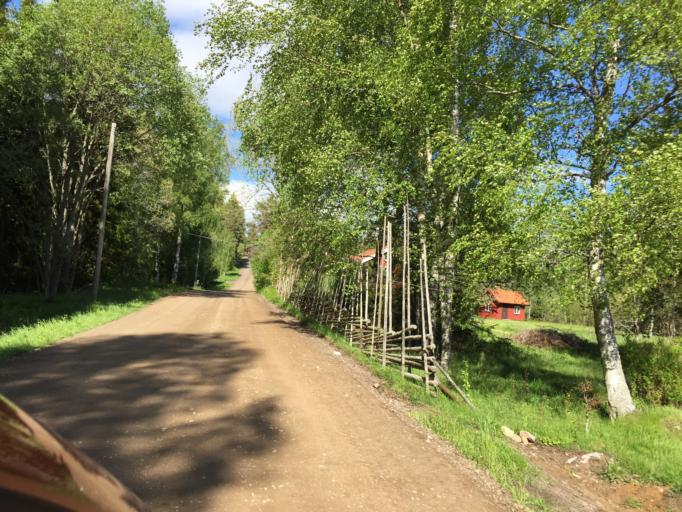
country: SE
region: Soedermanland
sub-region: Vingakers Kommun
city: Vingaker
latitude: 58.9930
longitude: 15.6685
